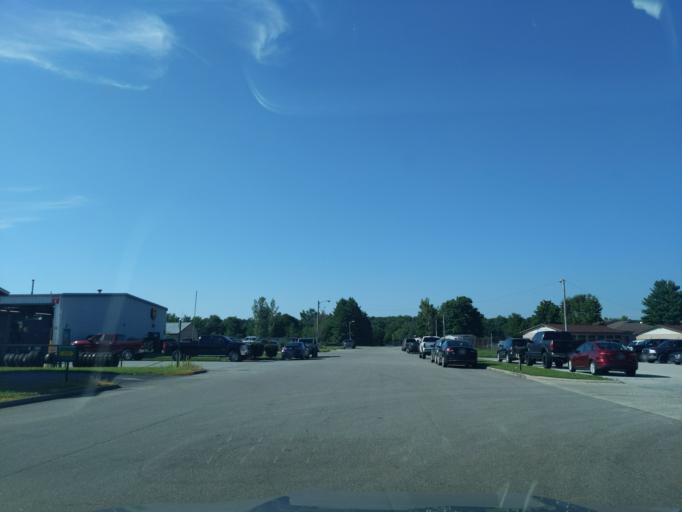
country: US
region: Indiana
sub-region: Ripley County
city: Versailles
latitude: 39.0712
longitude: -85.2643
